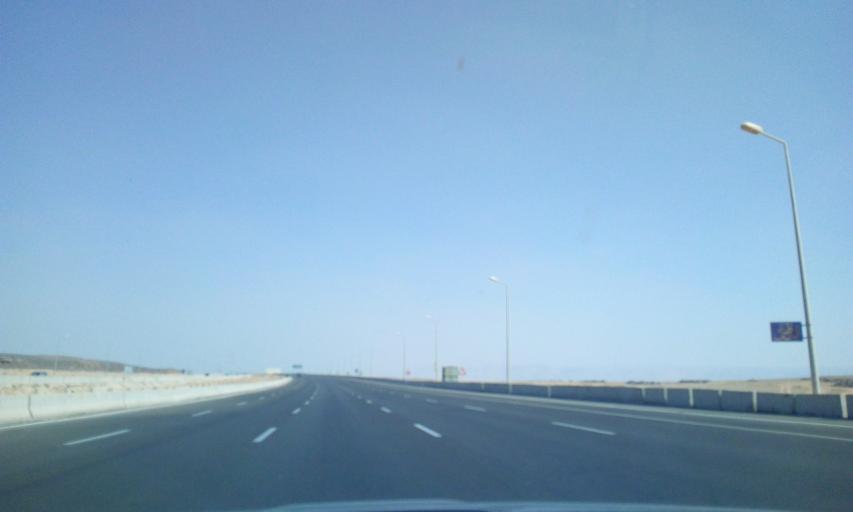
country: EG
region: As Suways
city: Ain Sukhna
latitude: 29.7193
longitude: 32.0597
